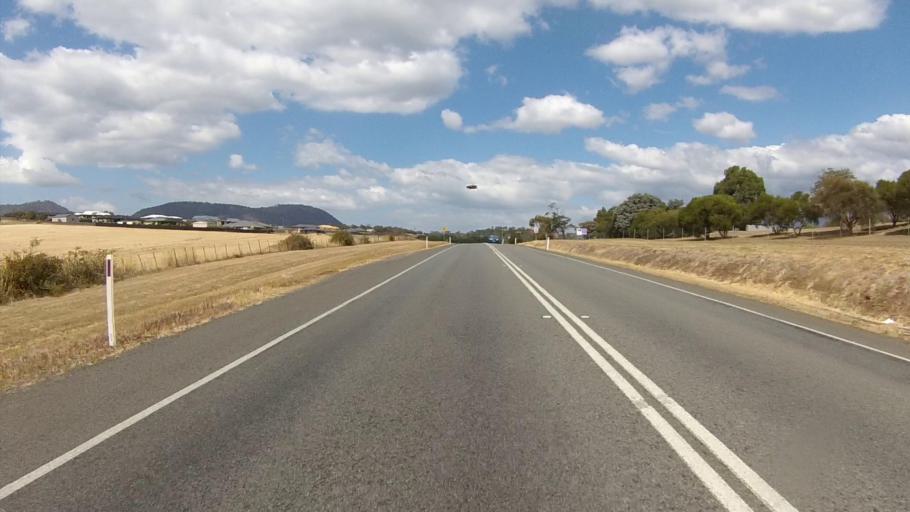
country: AU
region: Tasmania
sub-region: Brighton
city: Old Beach
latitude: -42.7603
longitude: 147.2682
